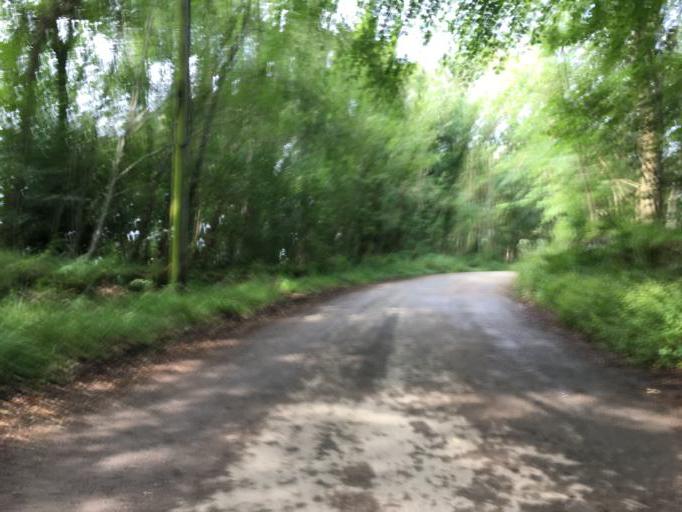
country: GB
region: Scotland
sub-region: West Lothian
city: Livingston
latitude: 55.8593
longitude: -3.5193
